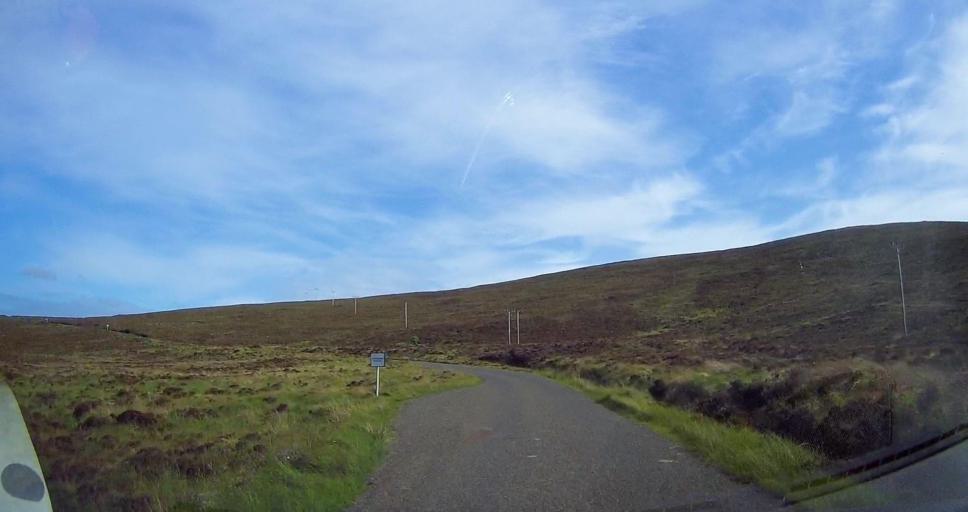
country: GB
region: Scotland
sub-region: Orkney Islands
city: Stromness
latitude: 58.8696
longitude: -3.2317
